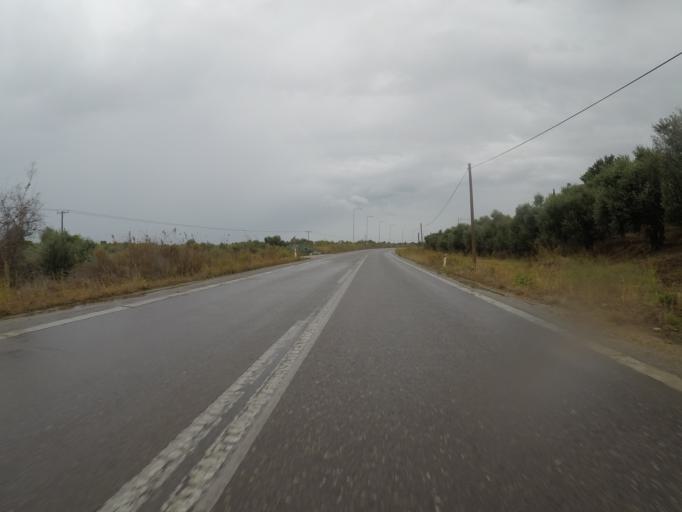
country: GR
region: West Greece
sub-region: Nomos Ileias
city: Zacharo
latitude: 37.4013
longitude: 21.6784
